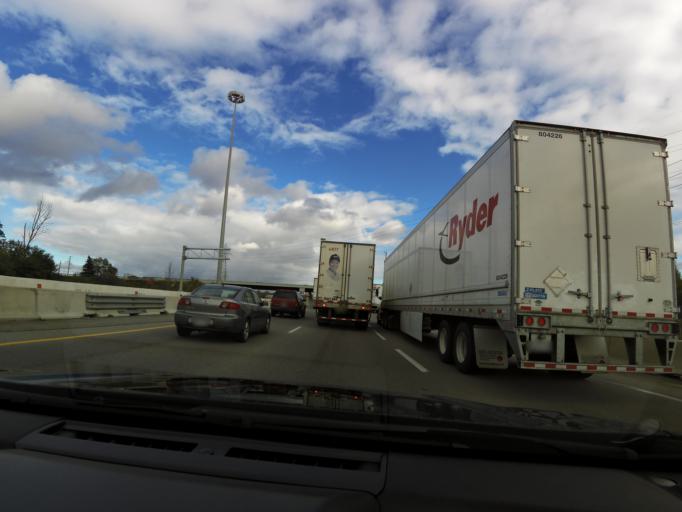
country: CA
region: Ontario
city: Cambridge
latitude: 43.4133
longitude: -80.3525
